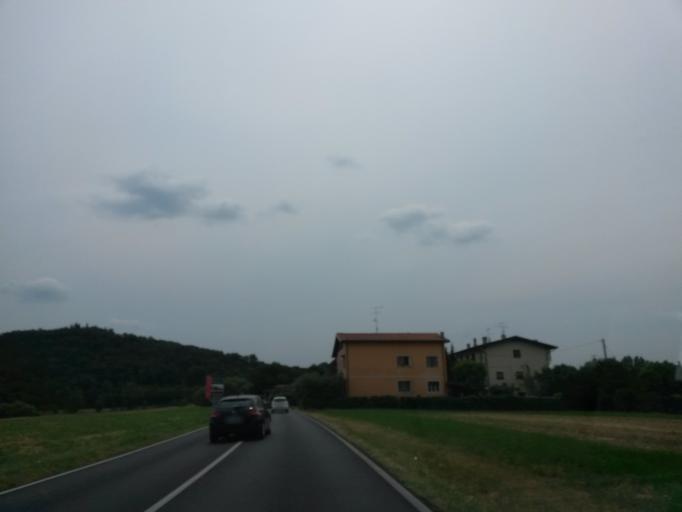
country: IT
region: Lombardy
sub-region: Provincia di Brescia
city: Padenghe sul Garda
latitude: 45.4886
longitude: 10.5151
